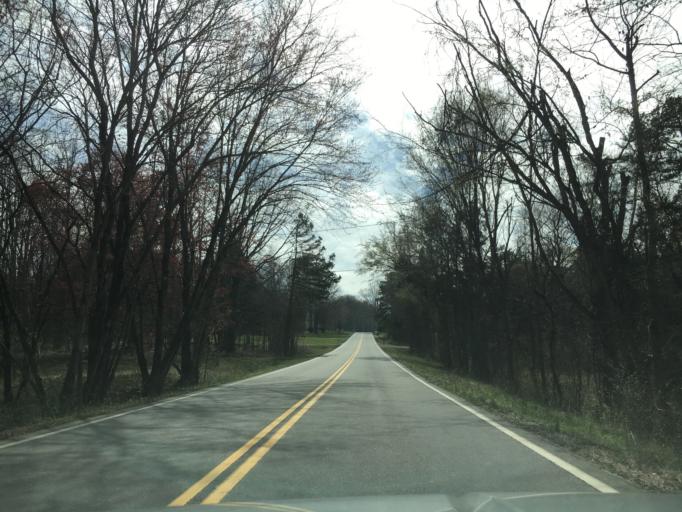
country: US
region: Virginia
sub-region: Halifax County
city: Halifax
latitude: 36.7517
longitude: -78.9201
